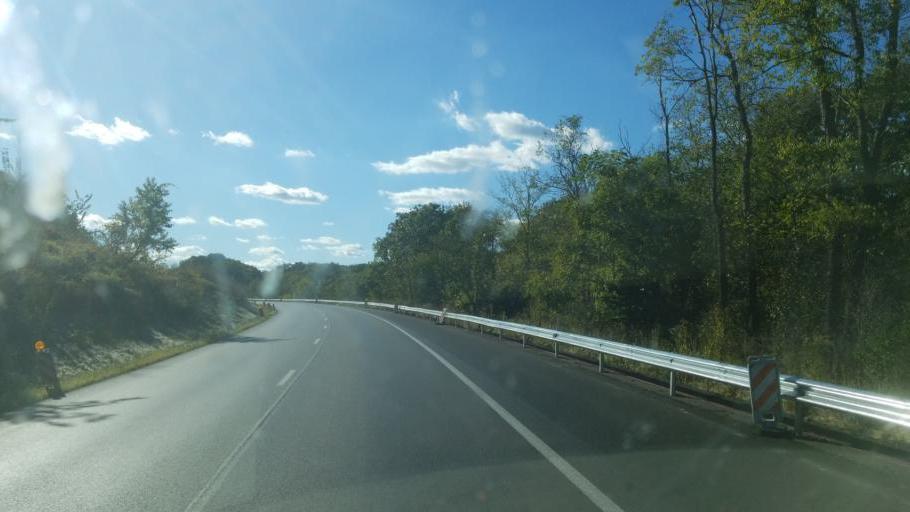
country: US
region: Pennsylvania
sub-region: Washington County
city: Wolfdale
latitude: 40.1253
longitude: -80.3746
